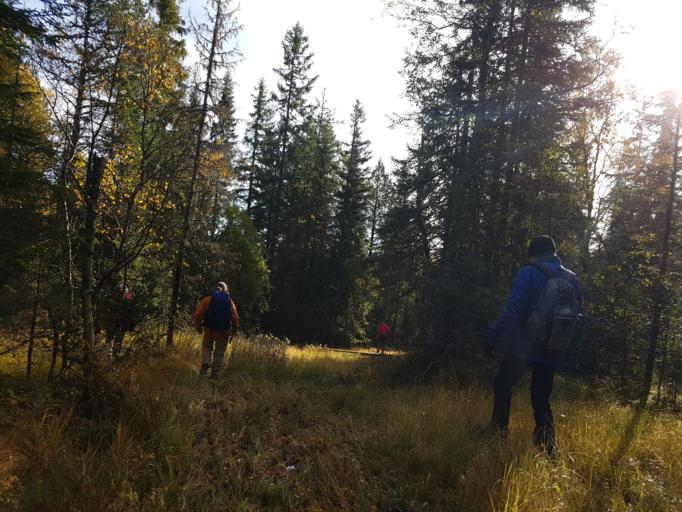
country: NO
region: Sor-Trondelag
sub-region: Trondheim
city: Trondheim
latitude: 63.4239
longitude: 10.2856
